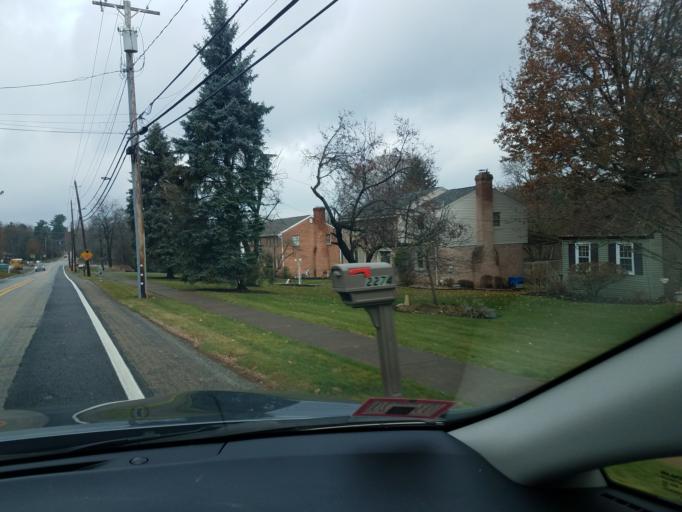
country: US
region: Pennsylvania
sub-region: Allegheny County
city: Franklin Park
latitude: 40.5735
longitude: -80.0740
